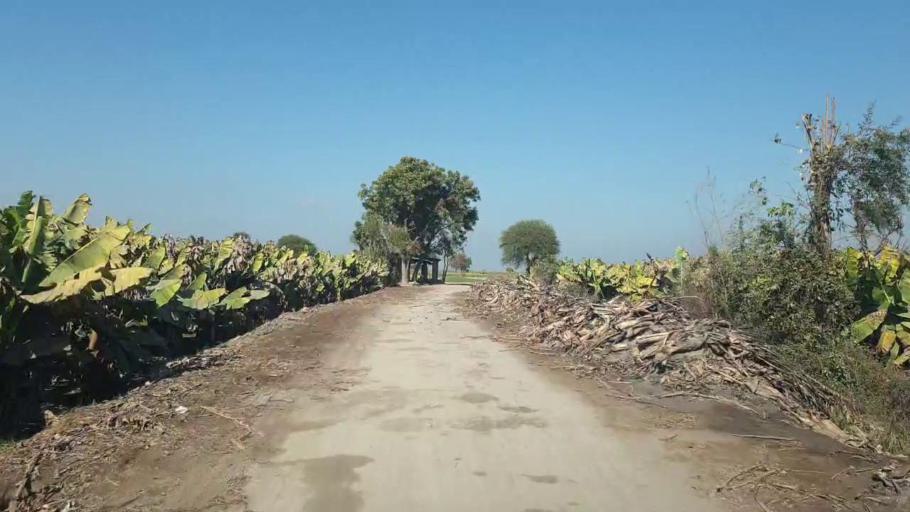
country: PK
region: Sindh
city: Shahdadpur
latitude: 25.9215
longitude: 68.5644
